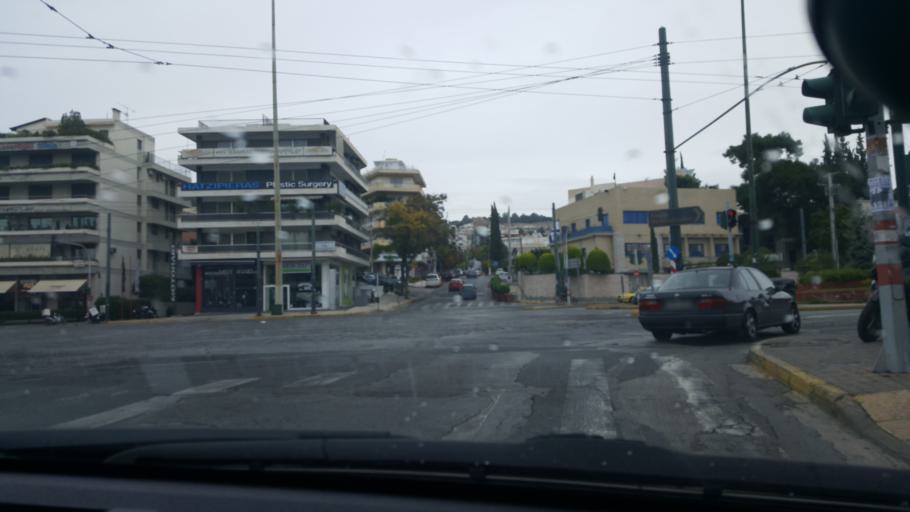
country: GR
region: Attica
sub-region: Nomarchia Athinas
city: Psychiko
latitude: 37.9978
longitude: 23.7695
